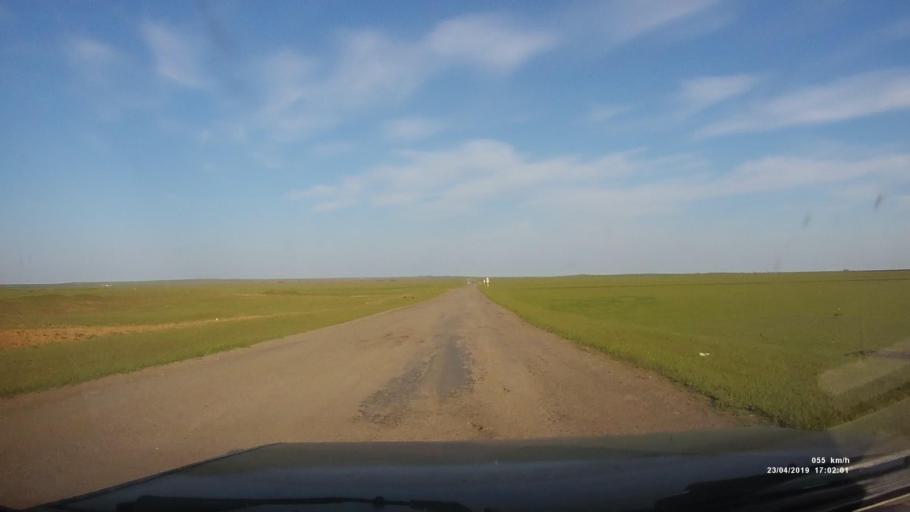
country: RU
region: Kalmykiya
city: Priyutnoye
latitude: 46.2938
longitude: 43.4128
